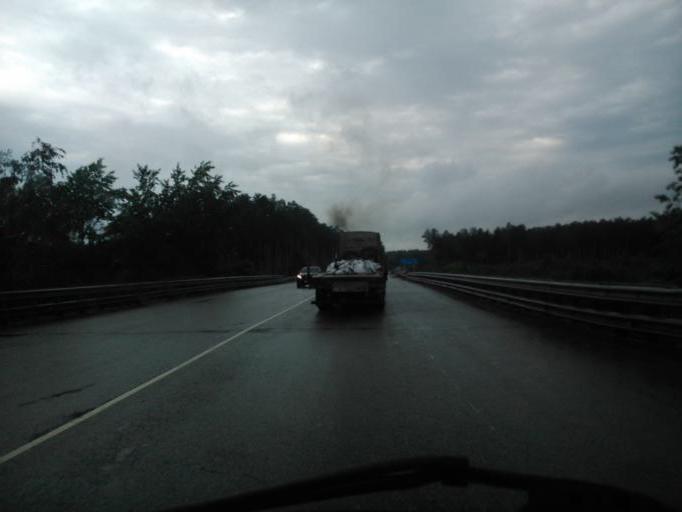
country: RU
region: Sverdlovsk
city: Beryozovsky
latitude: 56.8968
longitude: 60.7628
